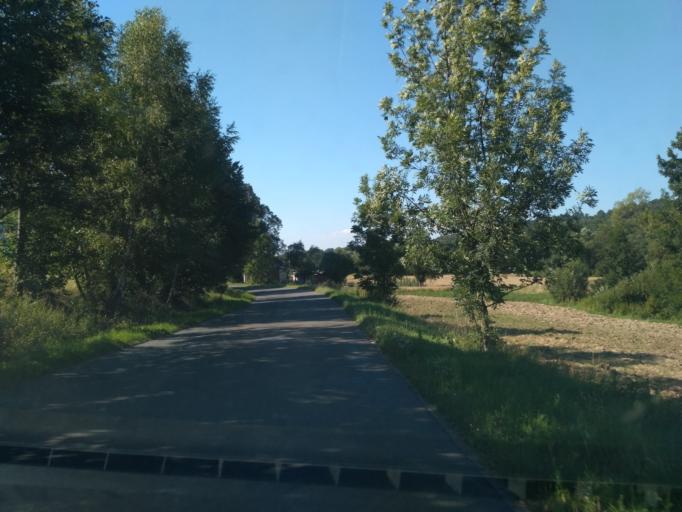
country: PL
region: Subcarpathian Voivodeship
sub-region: Powiat strzyzowski
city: Wysoka Strzyzowska
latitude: 49.8373
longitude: 21.7390
